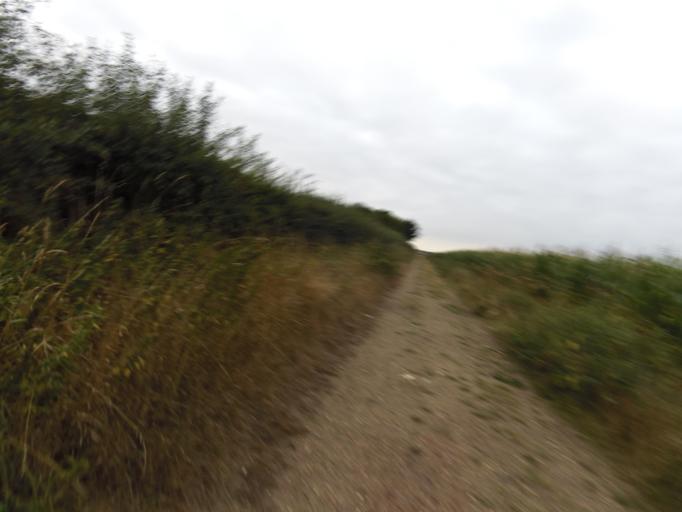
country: GB
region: England
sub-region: Hertfordshire
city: Radlett
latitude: 51.7179
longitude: -0.3157
